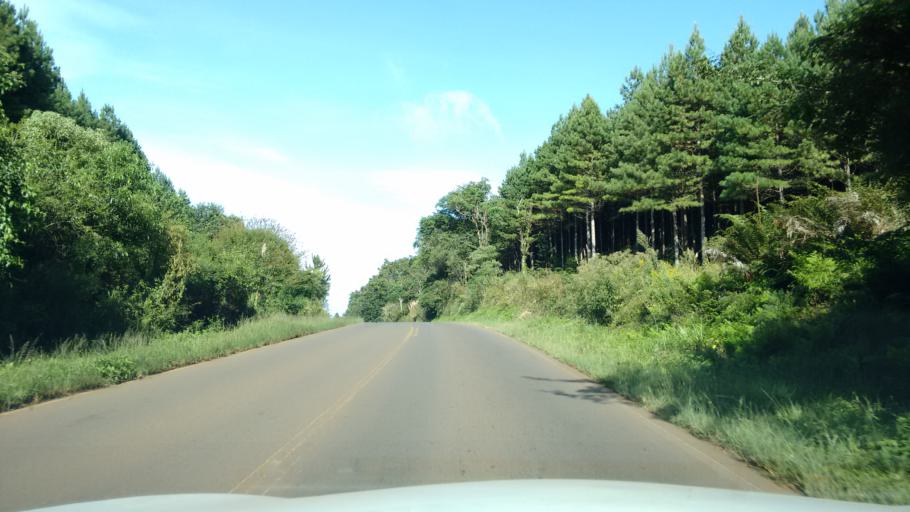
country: BR
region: Santa Catarina
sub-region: Videira
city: Videira
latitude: -27.1157
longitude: -50.9308
